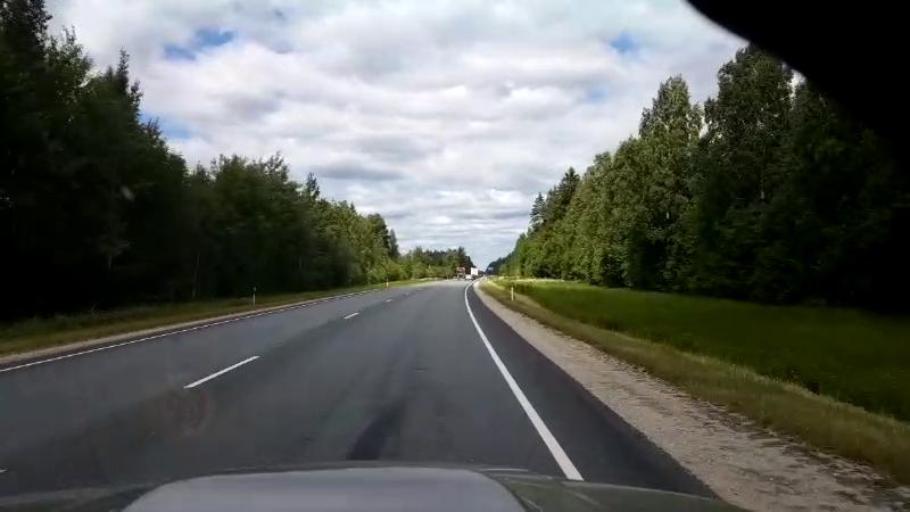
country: EE
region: Raplamaa
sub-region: Maerjamaa vald
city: Marjamaa
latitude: 58.7796
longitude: 24.4133
